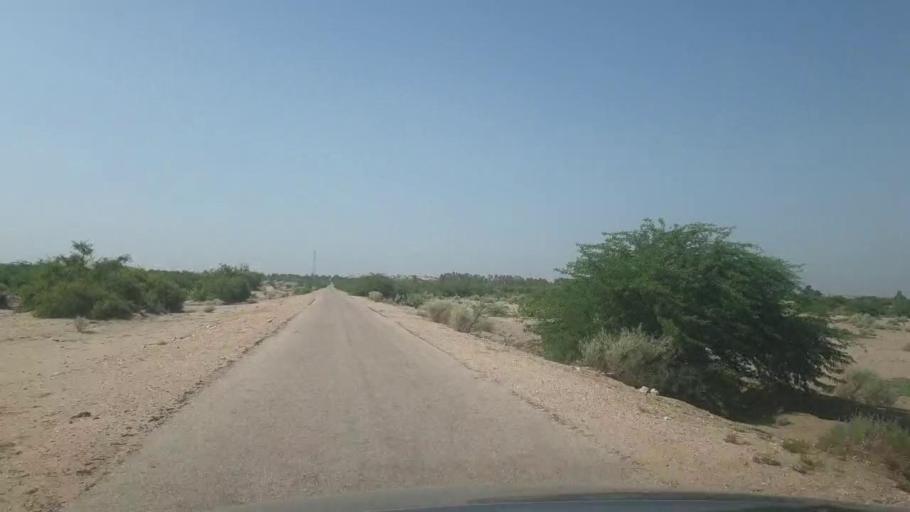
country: PK
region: Sindh
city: Rohri
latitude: 27.4193
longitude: 69.0799
